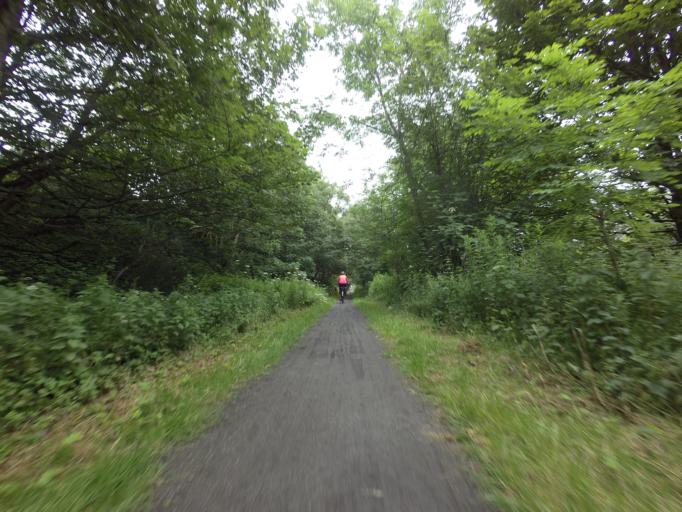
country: GB
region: Scotland
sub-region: Aberdeenshire
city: Mintlaw
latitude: 57.5191
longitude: -2.1288
